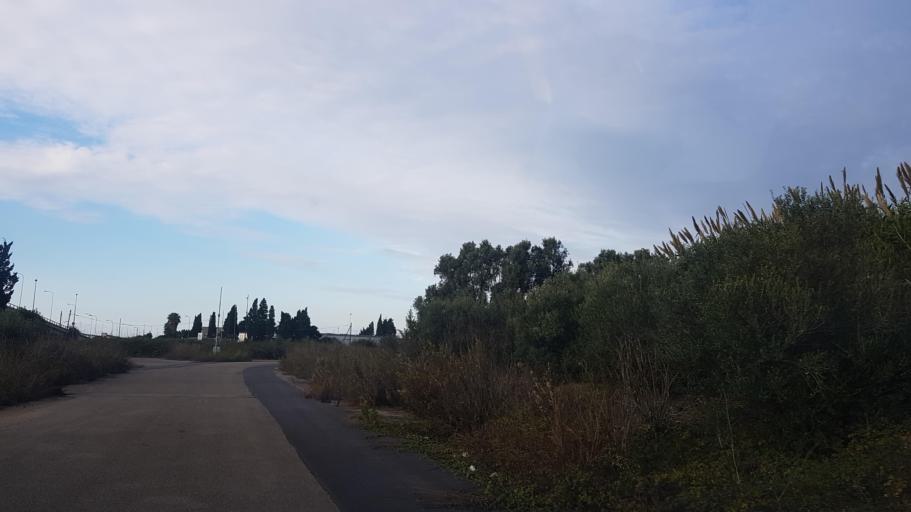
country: IT
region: Apulia
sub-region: Provincia di Brindisi
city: Materdomini
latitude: 40.6318
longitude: 17.9700
